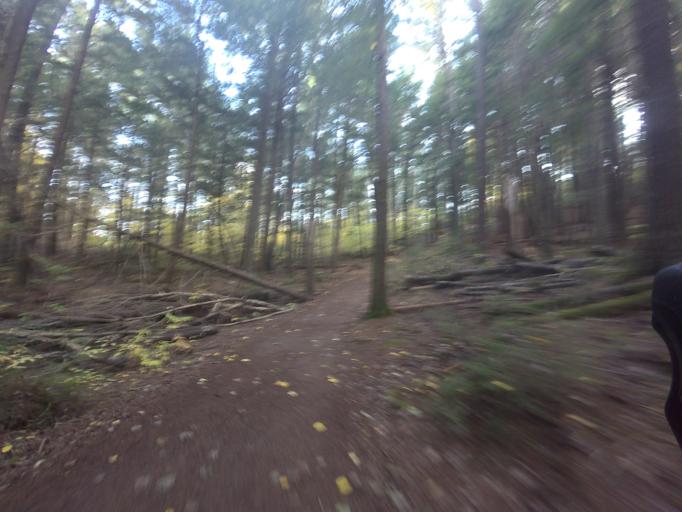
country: CA
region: Ontario
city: Deep River
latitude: 45.8875
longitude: -77.6334
